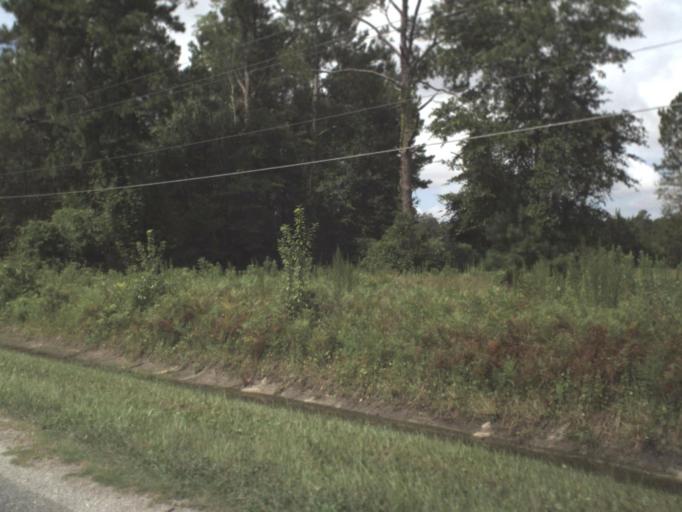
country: US
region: Florida
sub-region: Columbia County
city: Five Points
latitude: 30.2571
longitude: -82.6380
